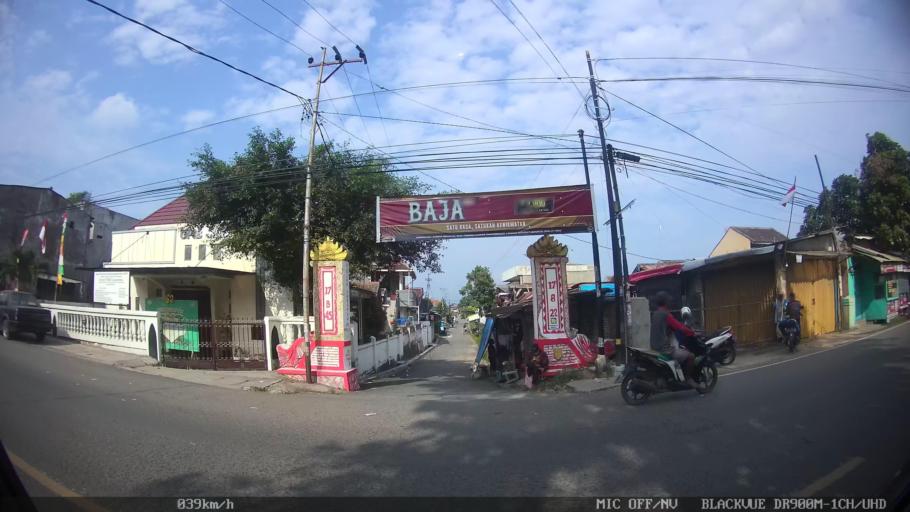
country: ID
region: Lampung
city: Panjang
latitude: -5.4779
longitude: 105.3231
